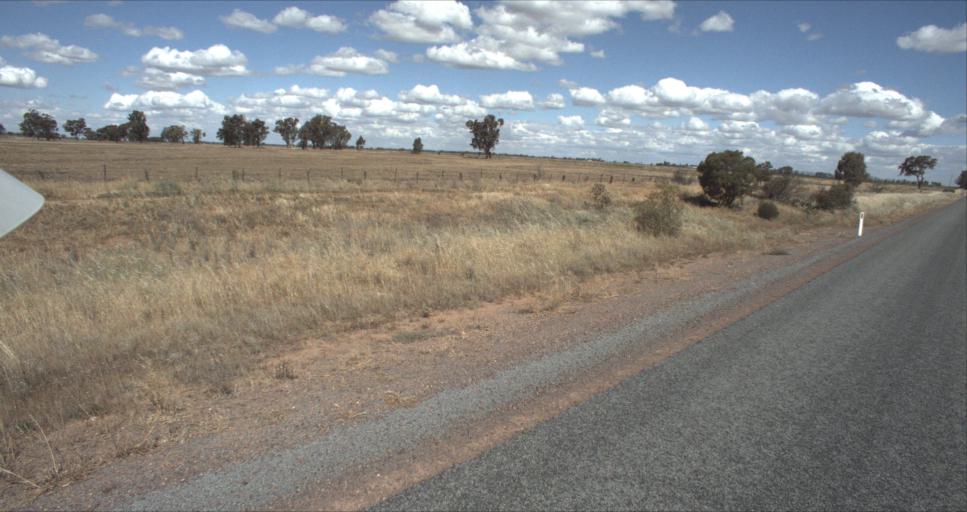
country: AU
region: New South Wales
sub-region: Leeton
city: Leeton
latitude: -34.4907
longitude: 146.2473
